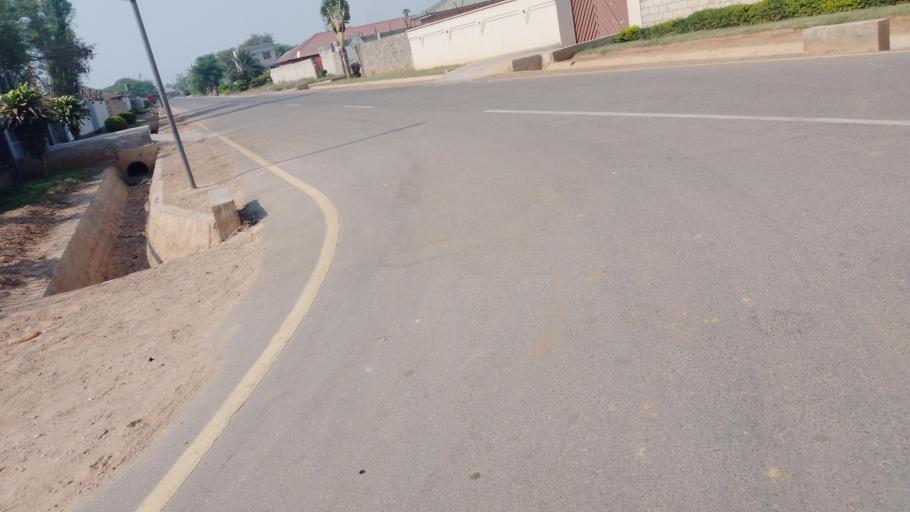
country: ZM
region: Lusaka
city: Lusaka
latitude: -15.3873
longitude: 28.3914
